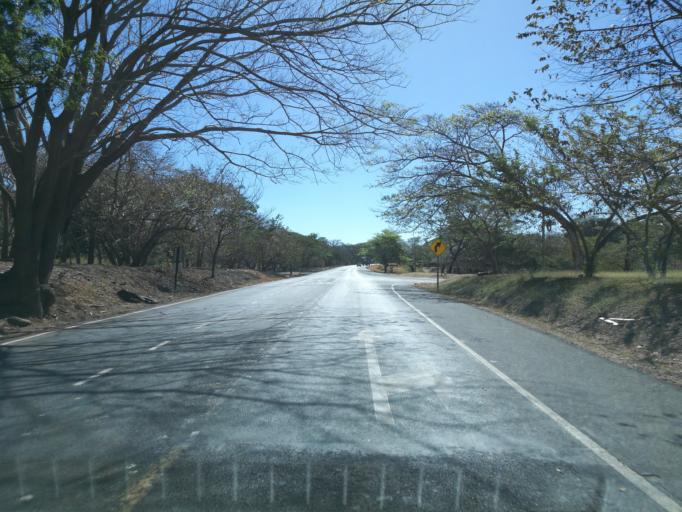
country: CR
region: Puntarenas
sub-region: Canton Central de Puntarenas
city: Puntarenas
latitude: 10.0974
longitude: -84.8603
